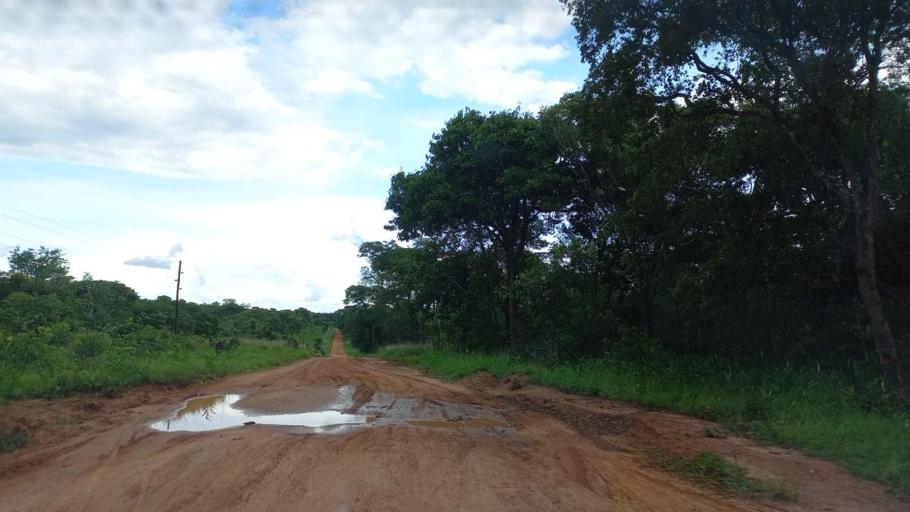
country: ZM
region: North-Western
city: Mwinilunga
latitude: -11.7907
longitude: 24.3726
